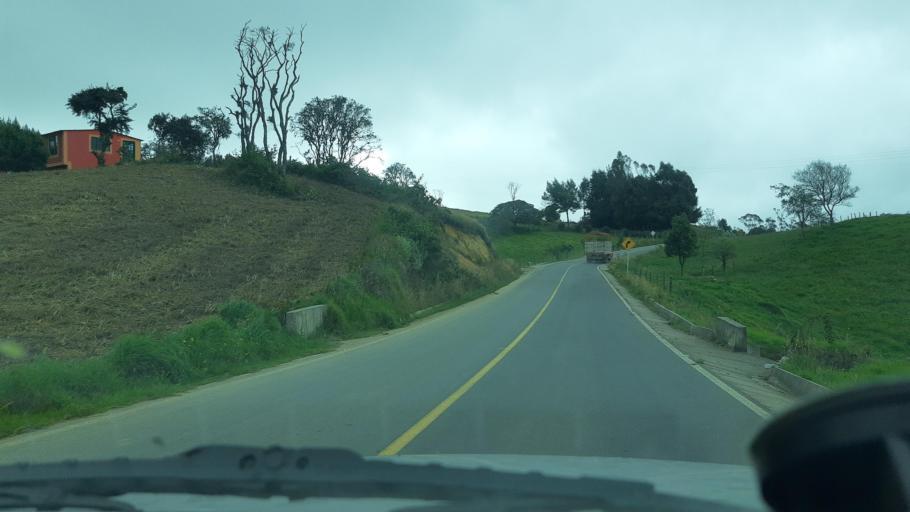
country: CO
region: Cundinamarca
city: Umbita
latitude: 5.2321
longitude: -73.4692
